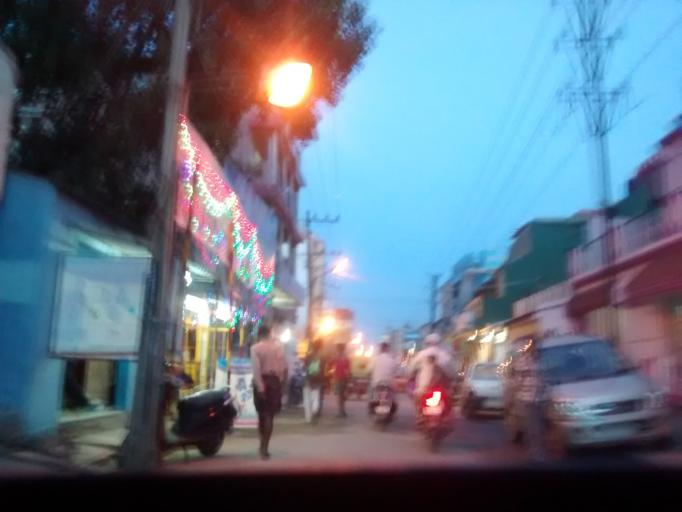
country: IN
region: Karnataka
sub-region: Bangalore Urban
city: Bangalore
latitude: 12.9677
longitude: 77.6697
